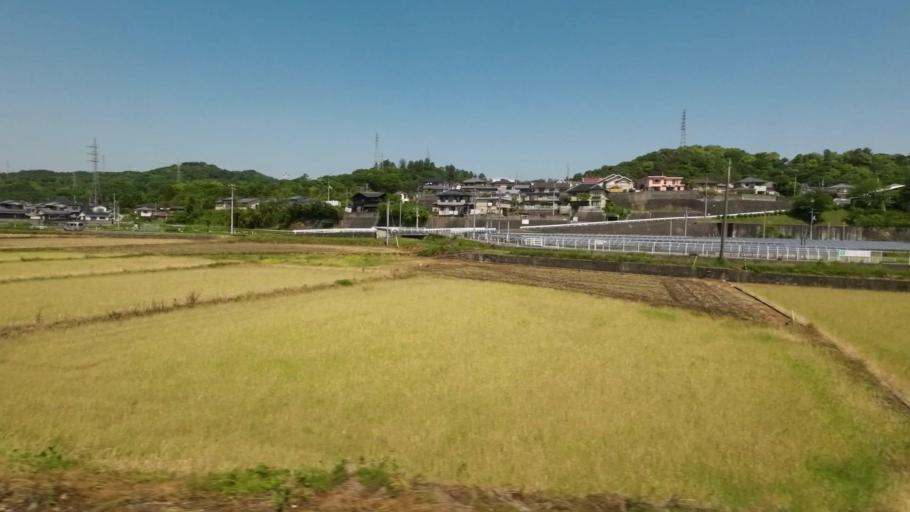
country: JP
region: Ehime
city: Niihama
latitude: 33.9299
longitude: 133.2695
